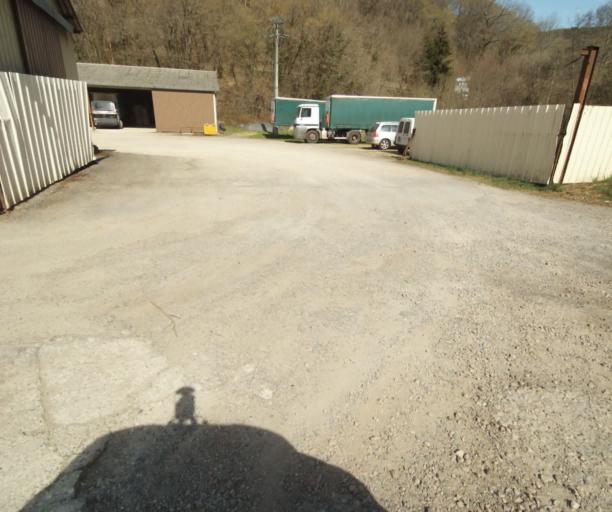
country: FR
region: Limousin
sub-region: Departement de la Correze
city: Naves
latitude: 45.3381
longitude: 1.7908
